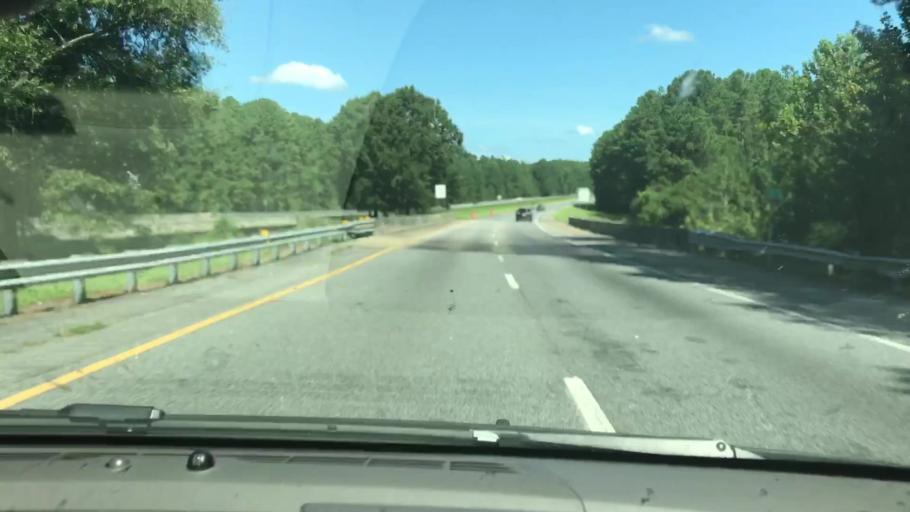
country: US
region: Georgia
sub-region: Harris County
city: Hamilton
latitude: 32.6370
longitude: -84.9676
